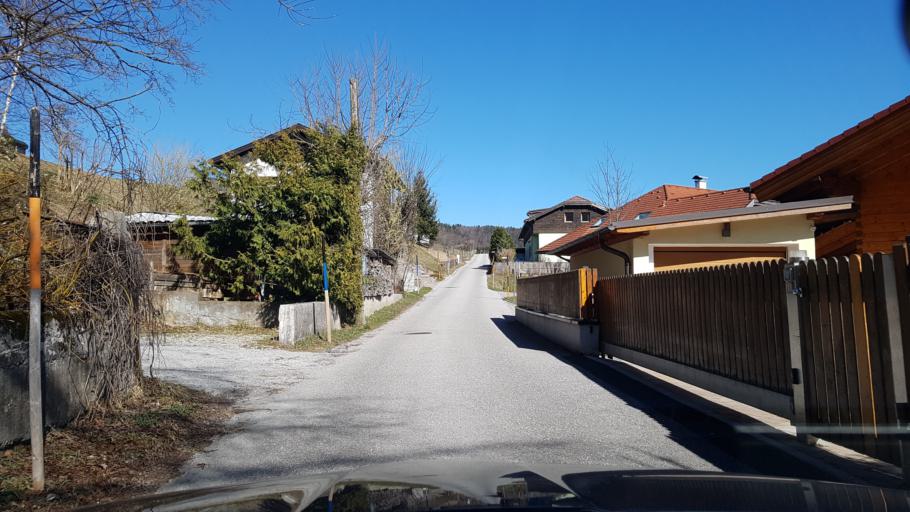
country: AT
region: Salzburg
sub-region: Politischer Bezirk Salzburg-Umgebung
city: Ebenau
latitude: 47.8054
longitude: 13.1736
